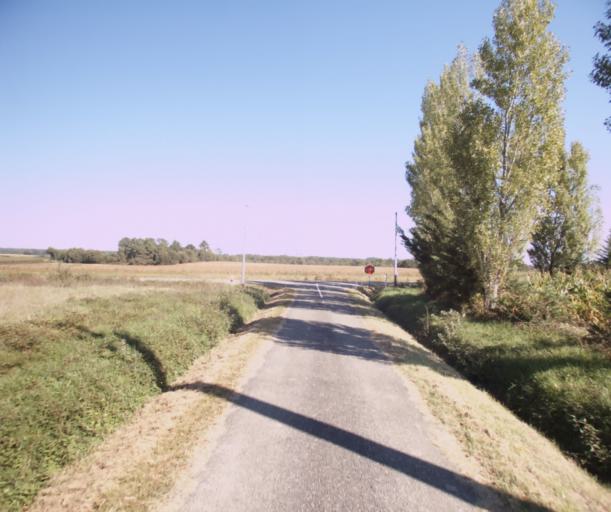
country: FR
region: Aquitaine
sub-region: Departement des Landes
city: Gabarret
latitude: 43.9505
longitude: 0.0012
